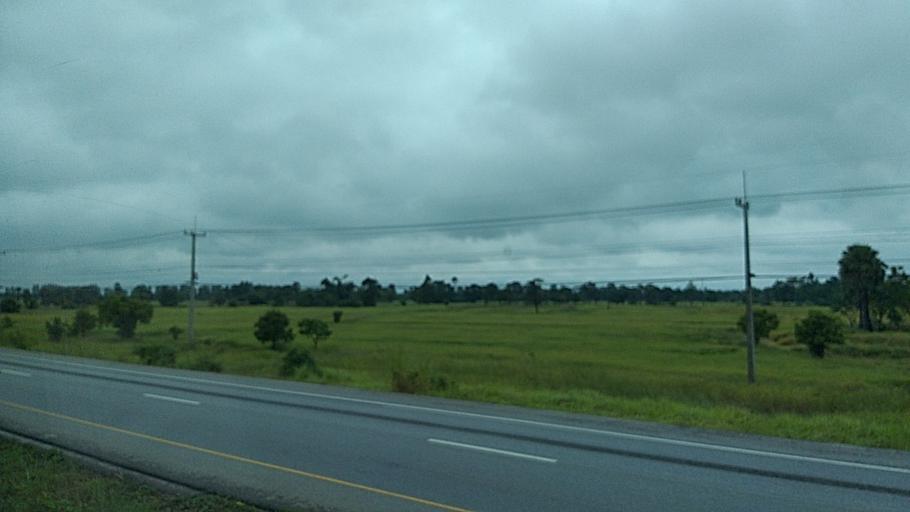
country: TH
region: Nakhon Ratchasima
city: Sida
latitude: 15.5088
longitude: 102.5337
